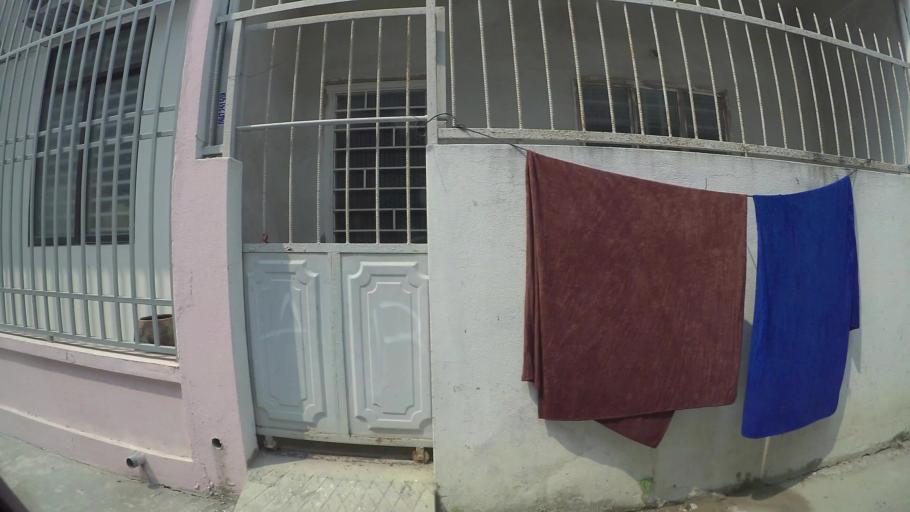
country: VN
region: Da Nang
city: Son Tra
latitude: 16.0395
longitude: 108.2204
